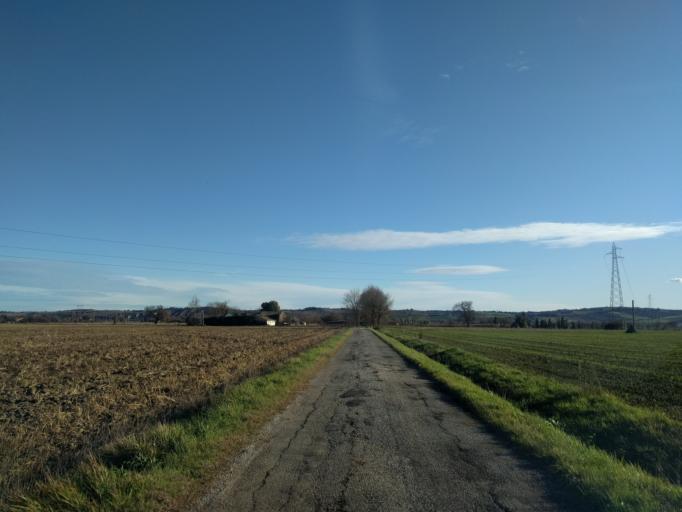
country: IT
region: The Marches
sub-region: Provincia di Pesaro e Urbino
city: Cuccurano
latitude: 43.7840
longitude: 12.9517
